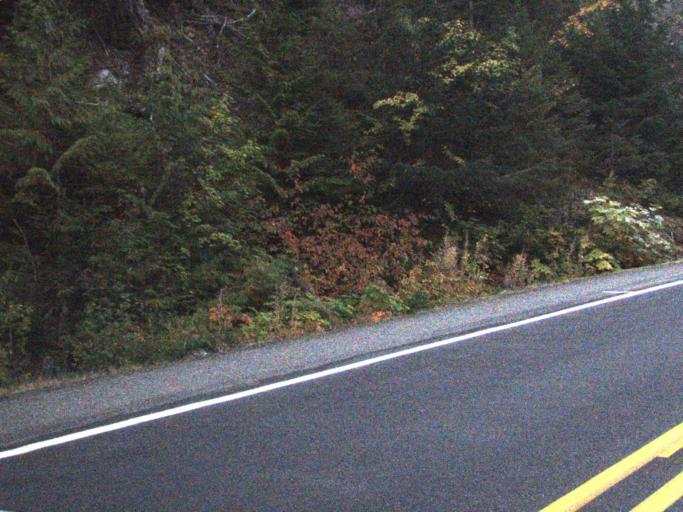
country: US
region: Washington
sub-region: Snohomish County
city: Darrington
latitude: 48.6921
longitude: -120.8933
